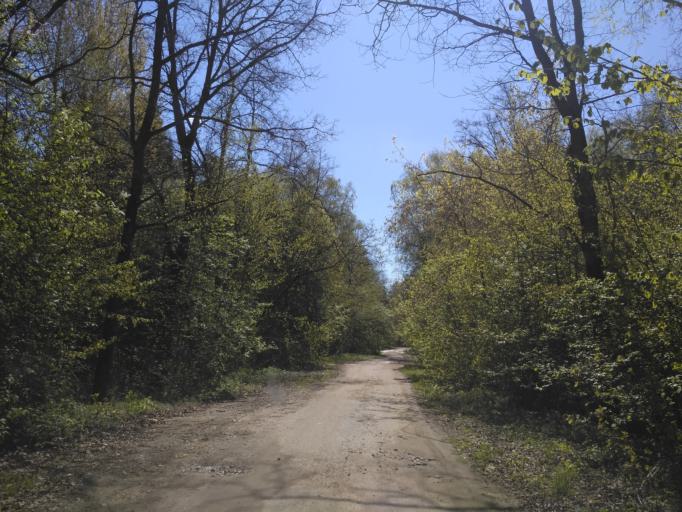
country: BY
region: Mogilev
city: Mstsislaw
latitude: 54.0484
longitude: 31.6973
